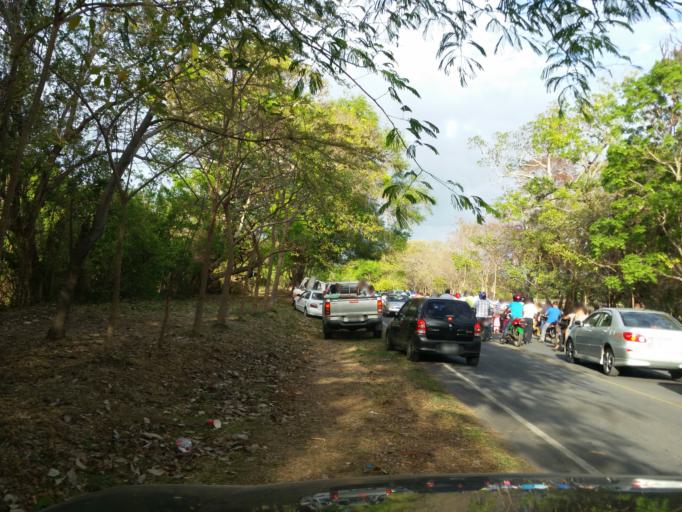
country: NI
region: Rivas
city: Rivas
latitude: 11.4421
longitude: -85.8476
